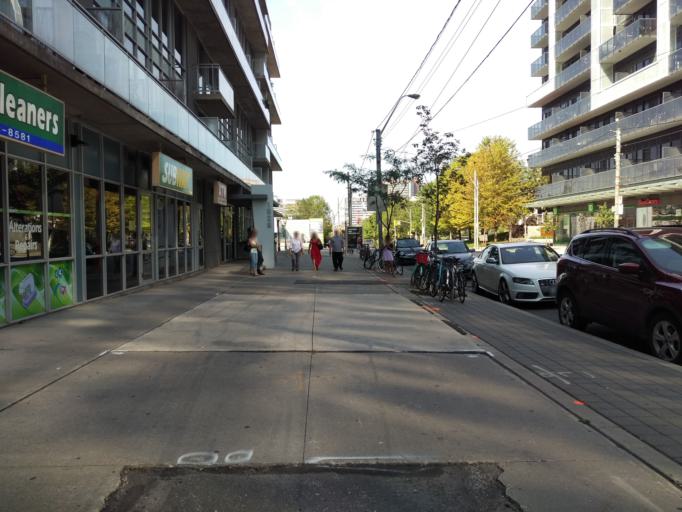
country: CA
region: Ontario
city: Toronto
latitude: 43.6413
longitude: -79.4157
